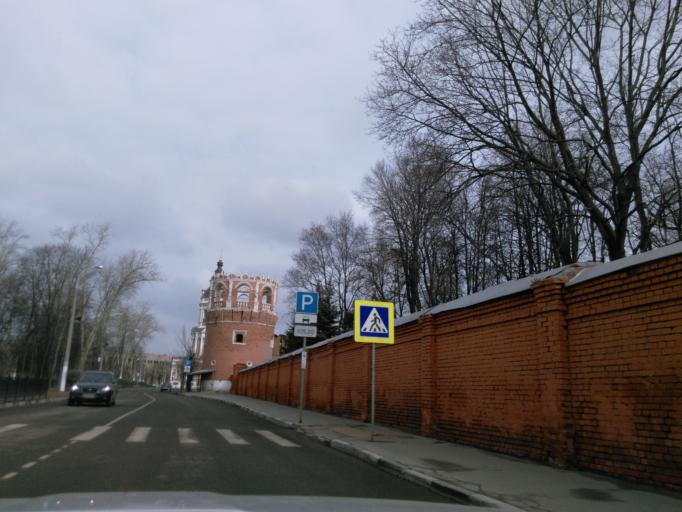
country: RU
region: Moscow
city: Novyye Cheremushki
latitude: 55.7124
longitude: 37.6006
